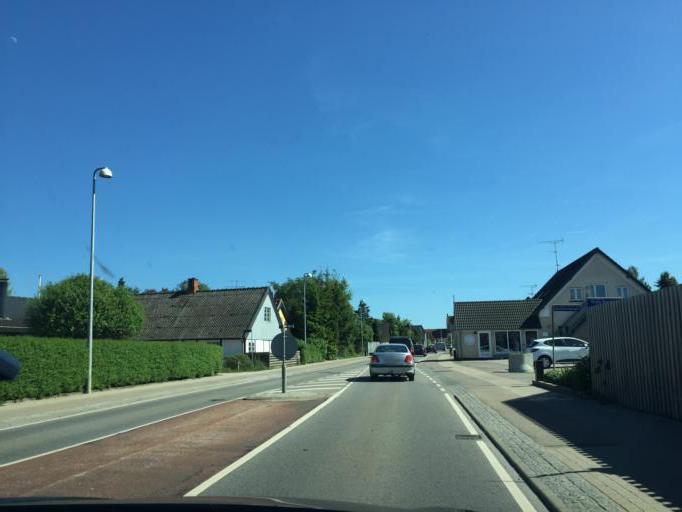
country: DK
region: Zealand
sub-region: Stevns Kommune
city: Stroby Egede
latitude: 55.3828
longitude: 12.2823
